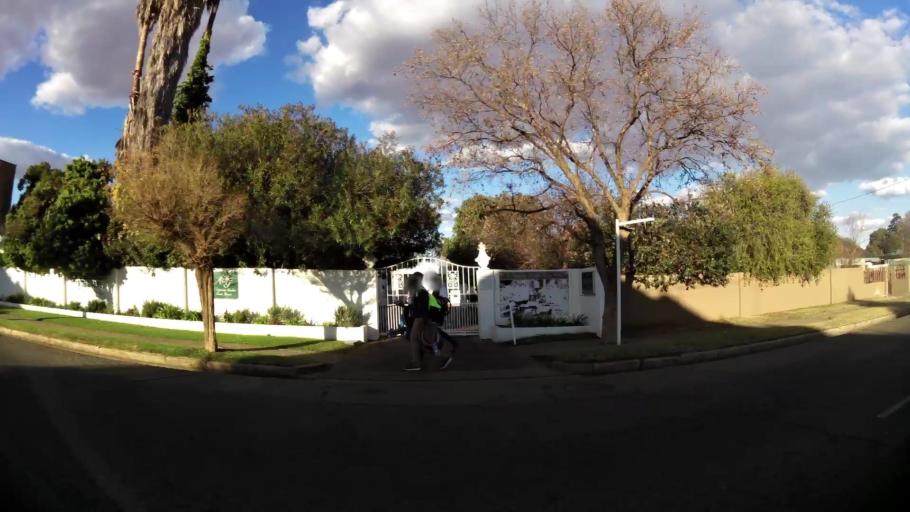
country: ZA
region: North-West
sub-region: Dr Kenneth Kaunda District Municipality
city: Potchefstroom
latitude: -26.7217
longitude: 27.0964
